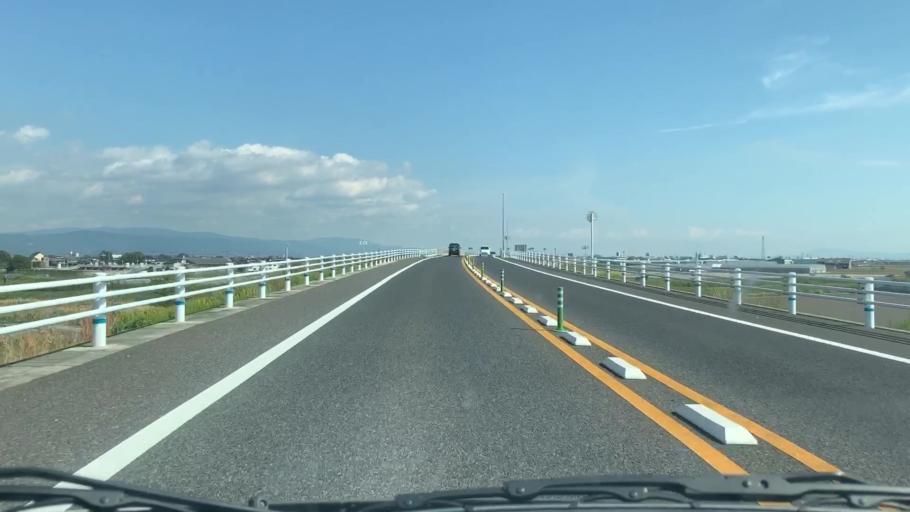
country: JP
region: Saga Prefecture
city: Saga-shi
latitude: 33.2281
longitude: 130.2206
